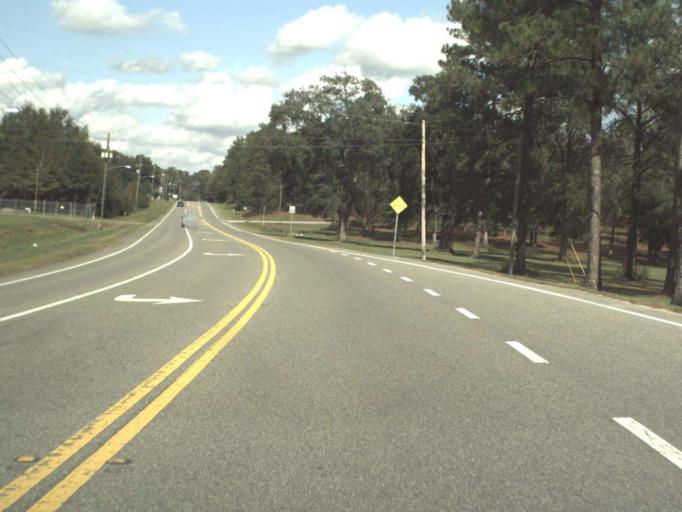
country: US
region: Florida
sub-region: Jackson County
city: Marianna
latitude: 30.7647
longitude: -85.2546
